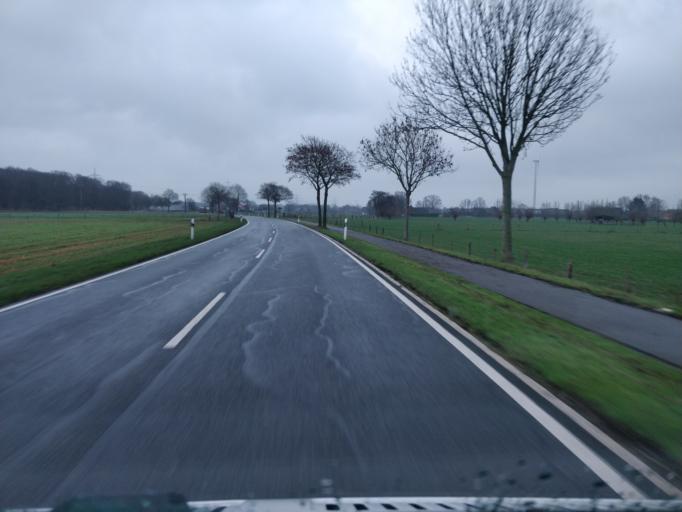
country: DE
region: North Rhine-Westphalia
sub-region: Regierungsbezirk Dusseldorf
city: Mehrhoog
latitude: 51.7584
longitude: 6.4993
